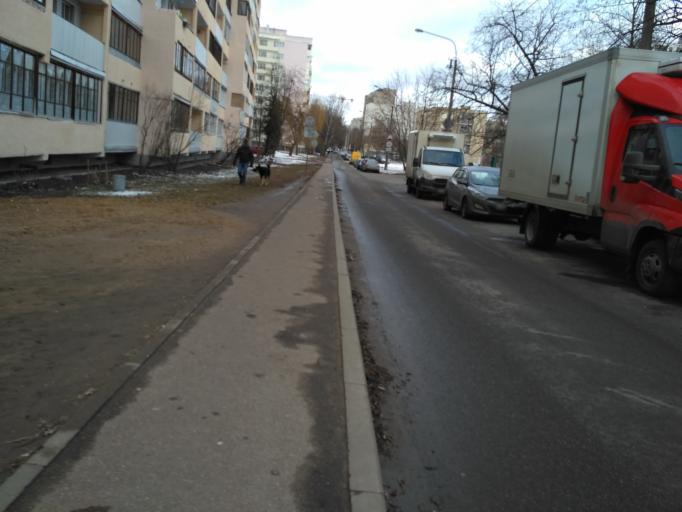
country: BY
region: Minsk
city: Minsk
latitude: 53.9233
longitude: 27.5831
